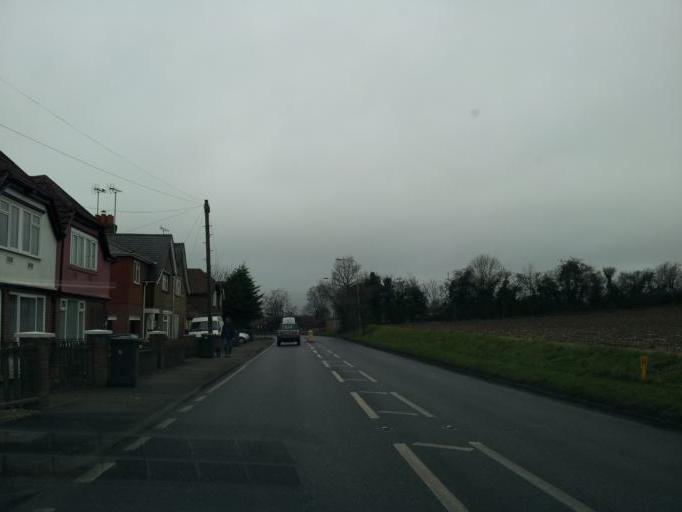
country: GB
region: England
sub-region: Essex
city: Manningtree
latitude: 51.9601
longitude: 1.0595
